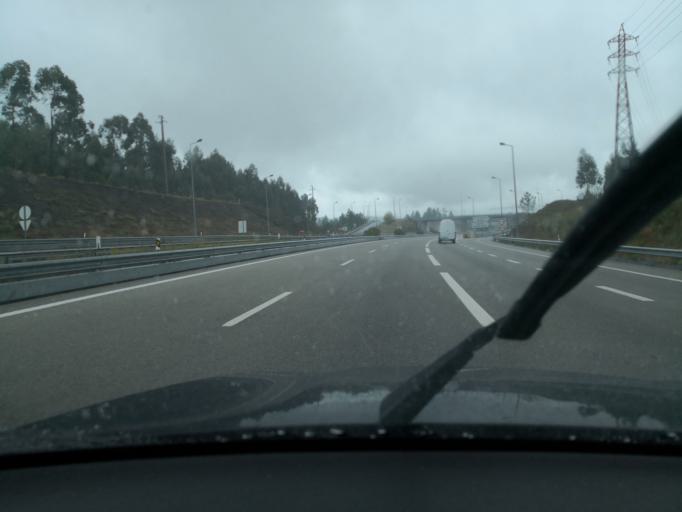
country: PT
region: Porto
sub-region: Pacos de Ferreira
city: Seroa
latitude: 41.2488
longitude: -8.4343
